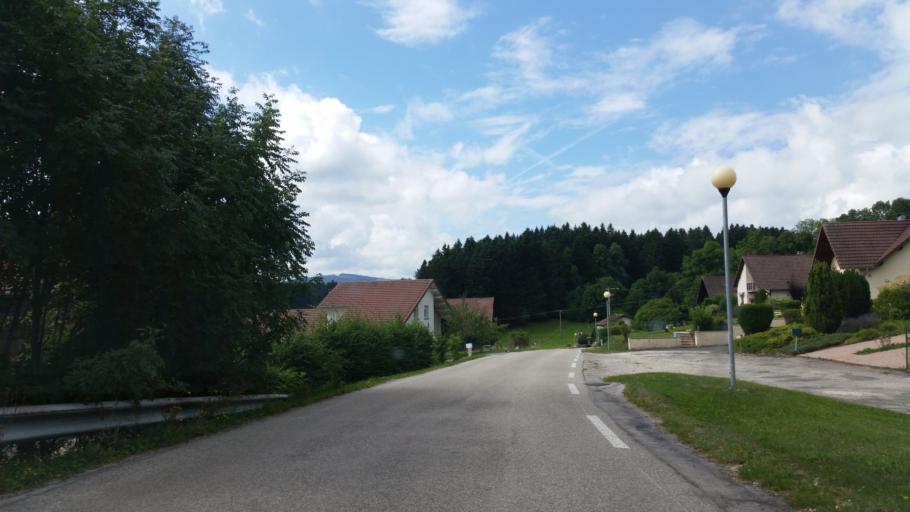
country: FR
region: Franche-Comte
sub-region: Departement du Doubs
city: Charquemont
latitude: 47.1677
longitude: 6.8285
